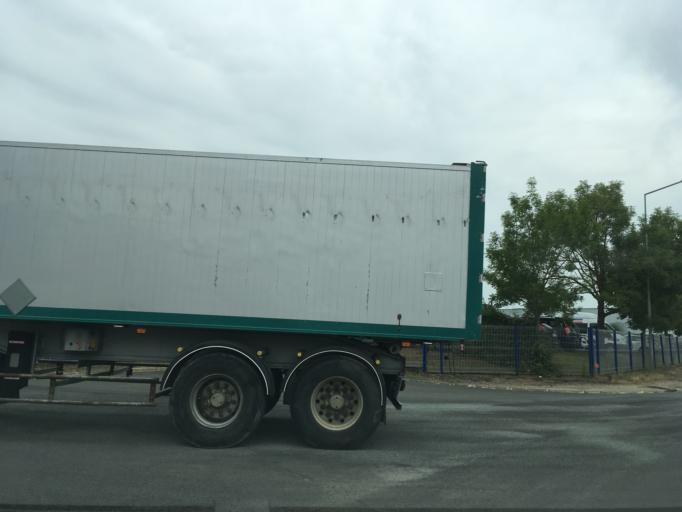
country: FR
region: Poitou-Charentes
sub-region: Departement des Deux-Sevres
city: Bessines
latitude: 46.3089
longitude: -0.4901
